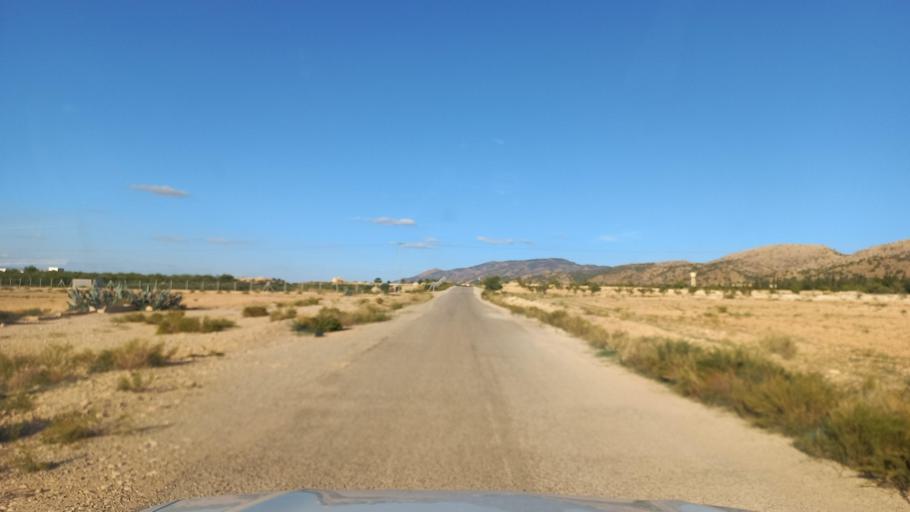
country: TN
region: Al Qasrayn
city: Sbiba
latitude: 35.3610
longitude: 9.1447
